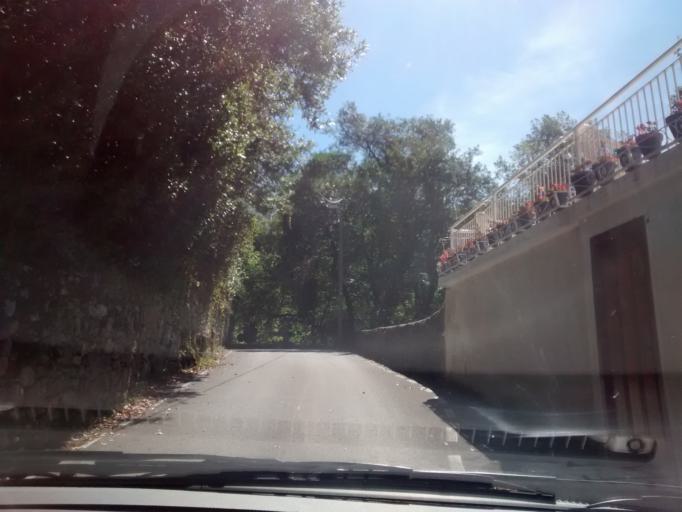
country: ES
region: Cantabria
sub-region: Provincia de Cantabria
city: Entrambasaguas
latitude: 43.3507
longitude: -3.7060
